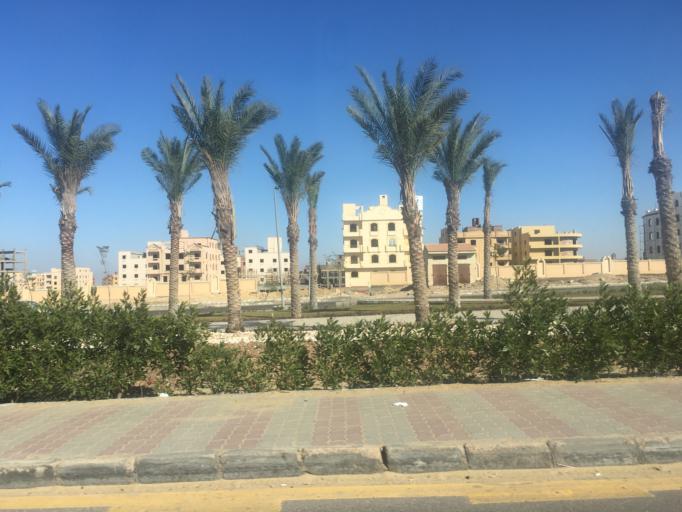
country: EG
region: Al Jizah
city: Awsim
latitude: 30.0144
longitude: 30.9771
